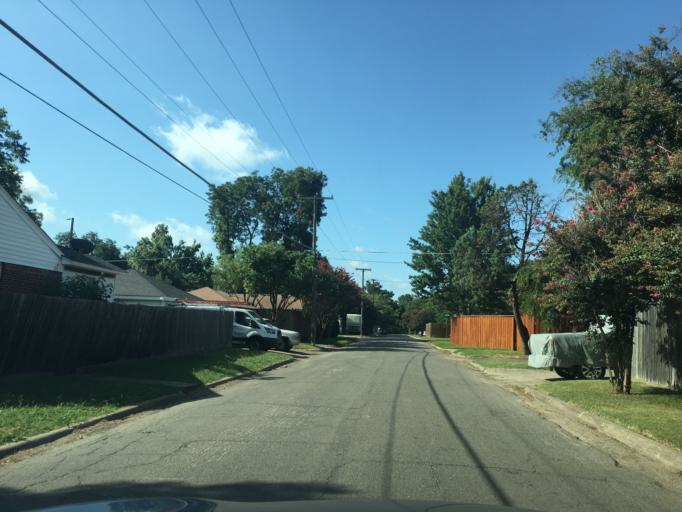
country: US
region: Texas
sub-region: Dallas County
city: Highland Park
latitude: 32.8355
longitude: -96.7583
